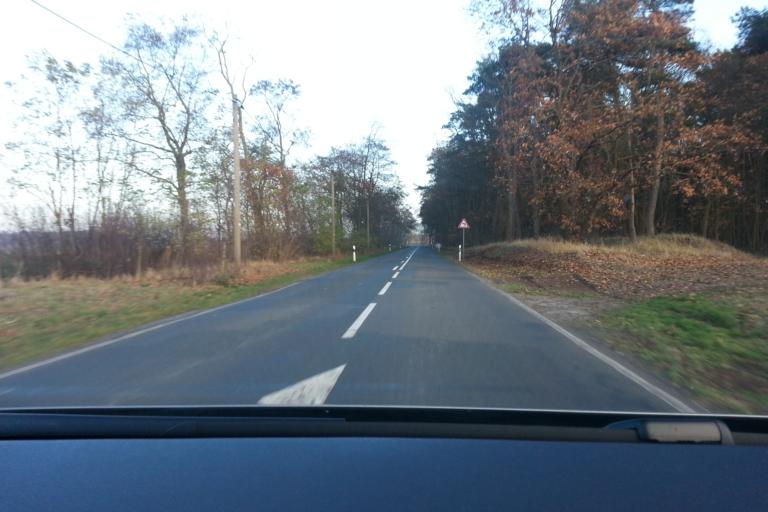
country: DE
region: Mecklenburg-Vorpommern
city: Ferdinandshof
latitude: 53.6346
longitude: 13.8374
